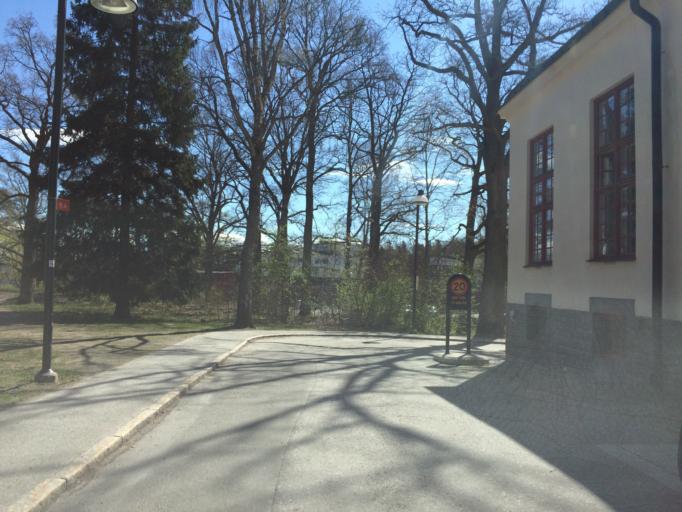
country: SE
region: Stockholm
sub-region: Huddinge Kommun
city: Huddinge
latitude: 59.2793
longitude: 17.9755
